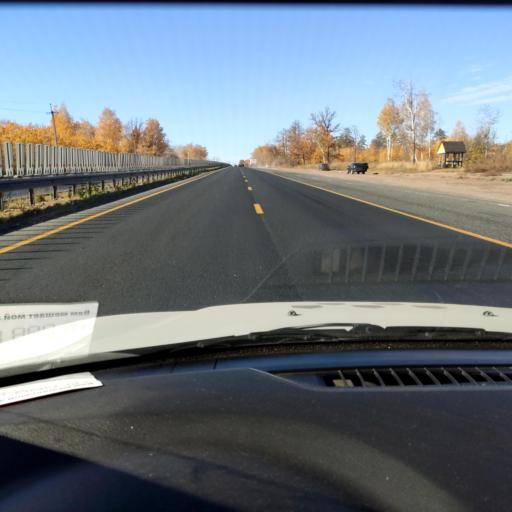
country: RU
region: Samara
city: Pribrezhnyy
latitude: 53.5119
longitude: 49.9267
